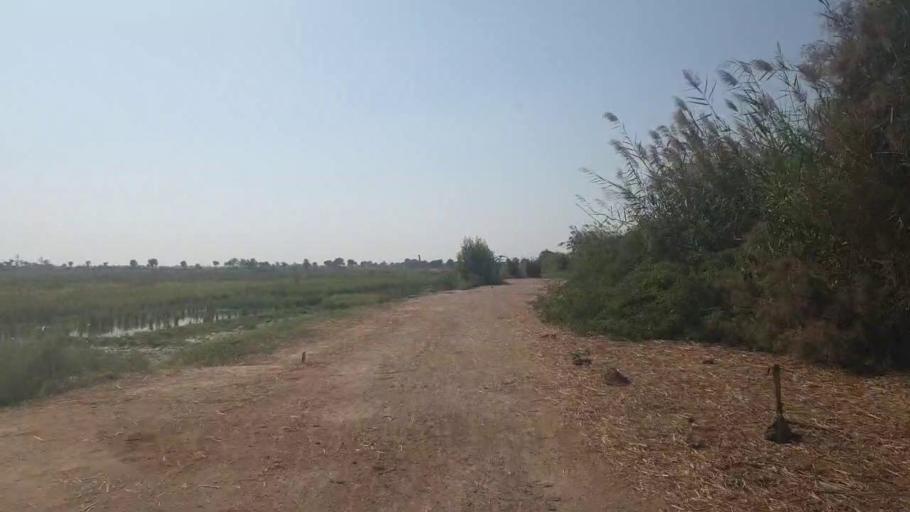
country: PK
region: Sindh
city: Badin
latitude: 24.5439
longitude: 68.8415
